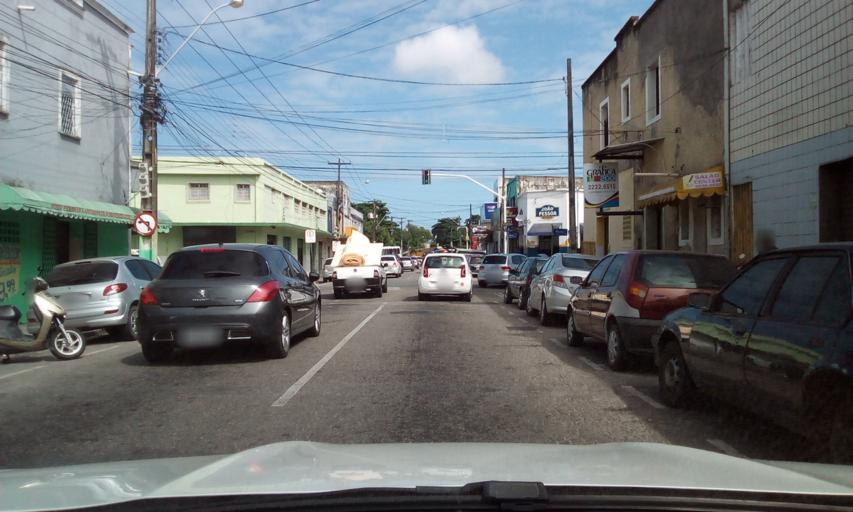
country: BR
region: Paraiba
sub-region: Joao Pessoa
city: Joao Pessoa
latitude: -7.1236
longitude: -34.8818
